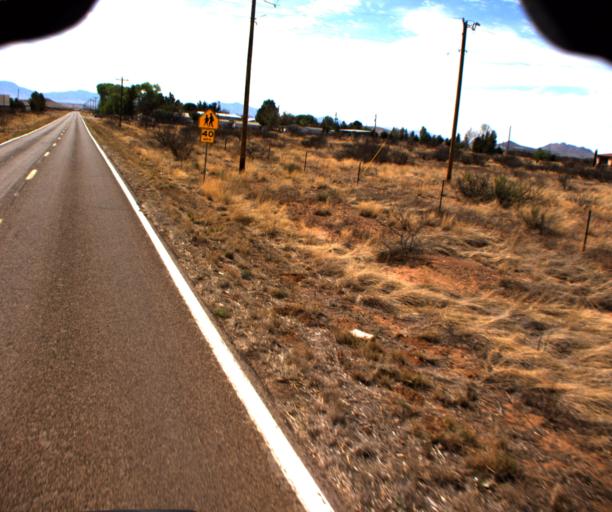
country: US
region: Arizona
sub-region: Cochise County
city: Willcox
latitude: 31.8763
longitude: -109.6333
